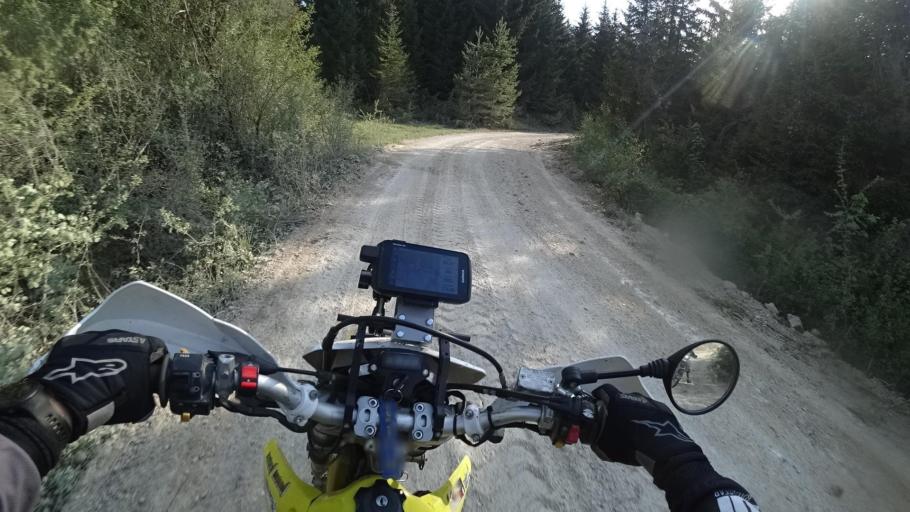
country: BA
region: Federation of Bosnia and Herzegovina
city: Glamoc
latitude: 44.0703
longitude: 16.7759
